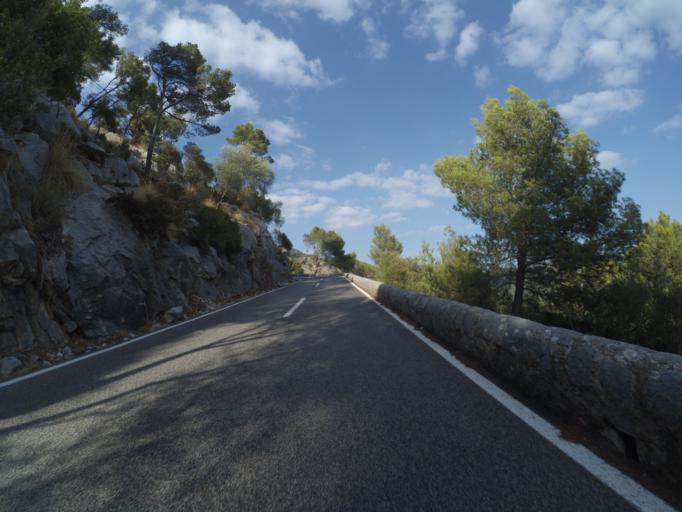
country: ES
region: Balearic Islands
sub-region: Illes Balears
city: Escorca
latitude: 39.7950
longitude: 2.8958
